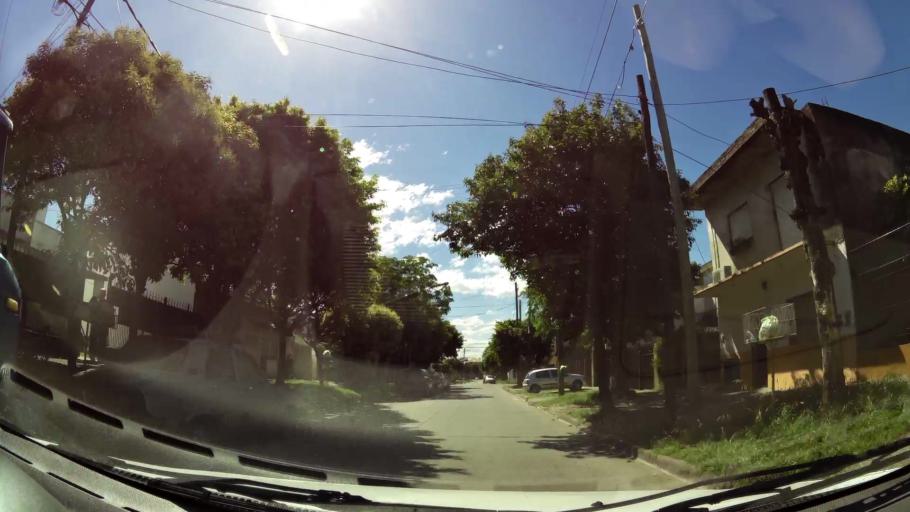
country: AR
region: Buenos Aires
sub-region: Partido de General San Martin
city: General San Martin
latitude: -34.5224
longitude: -58.5690
